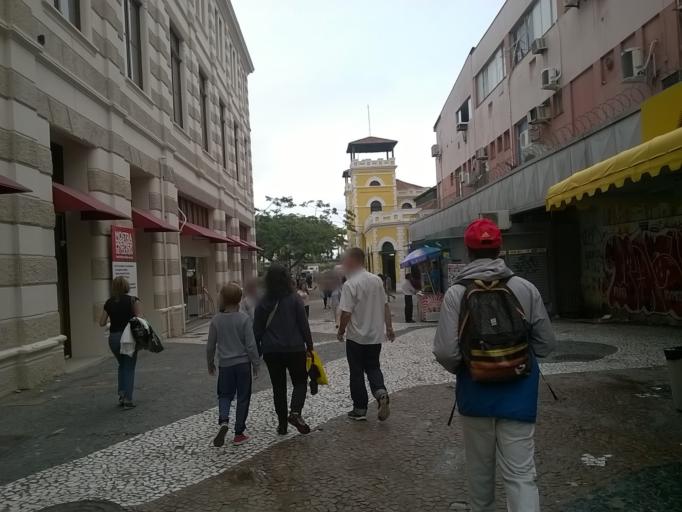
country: BR
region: Santa Catarina
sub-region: Florianopolis
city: Florianopolis
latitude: -27.5969
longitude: -48.5520
